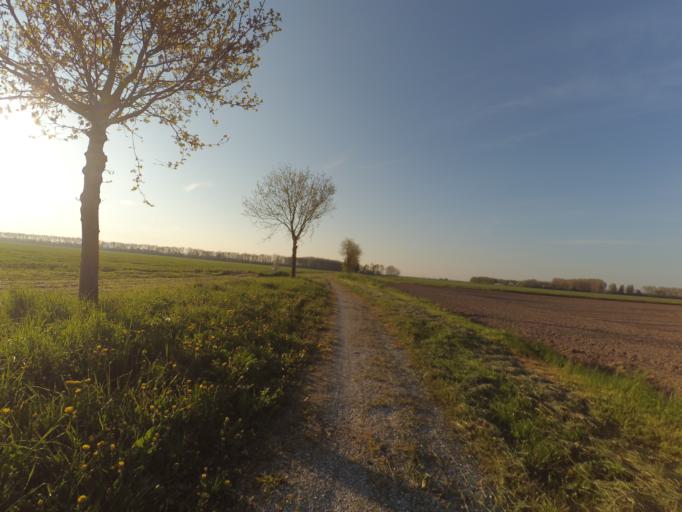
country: NL
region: Flevoland
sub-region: Gemeente Lelystad
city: Lelystad
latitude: 52.4588
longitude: 5.4979
